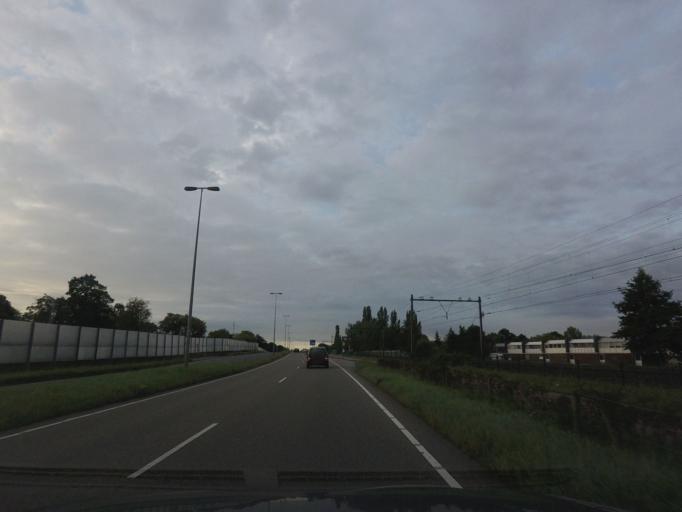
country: NL
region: North Holland
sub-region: Gemeente Zaanstad
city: Zaanstad
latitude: 52.4769
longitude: 4.8050
